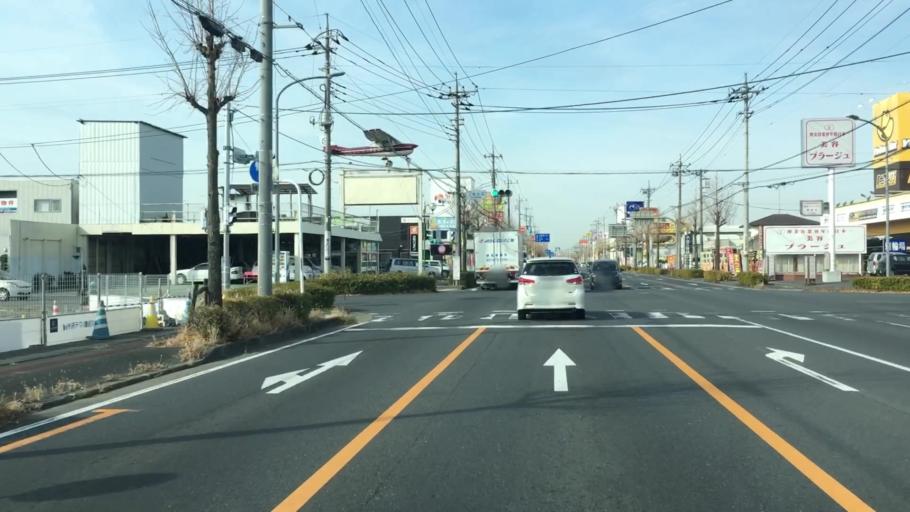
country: JP
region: Gunma
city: Tatebayashi
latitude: 36.2336
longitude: 139.5449
